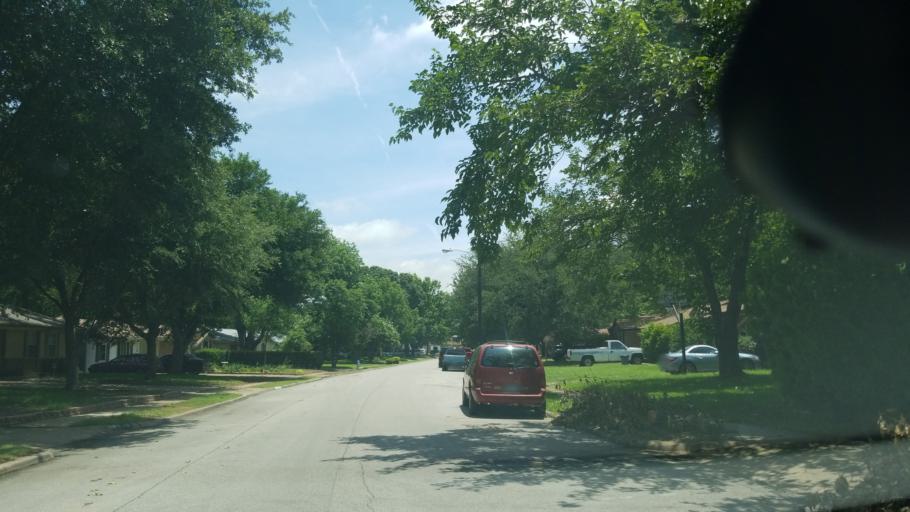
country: US
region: Texas
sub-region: Dallas County
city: Irving
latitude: 32.8496
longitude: -96.9706
